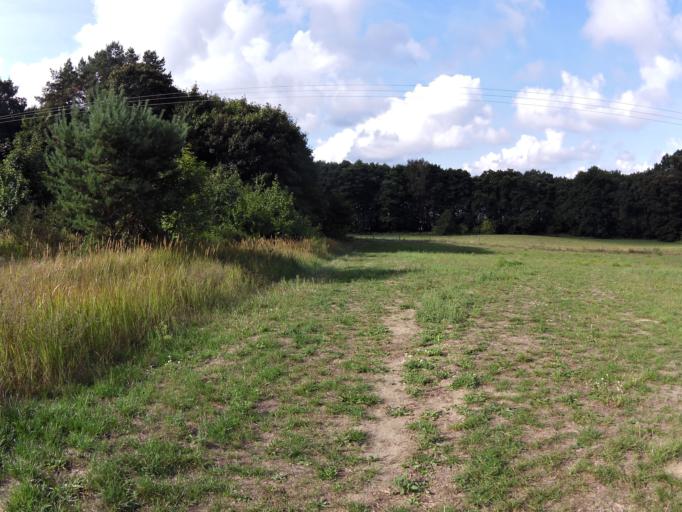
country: DE
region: Mecklenburg-Vorpommern
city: Seebad Bansin
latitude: 53.9667
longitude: 14.1215
